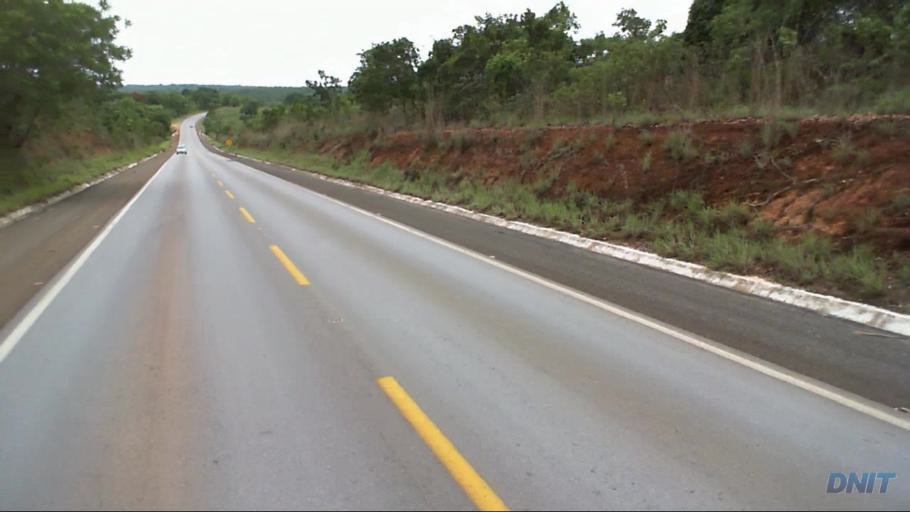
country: BR
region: Goias
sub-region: Uruacu
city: Uruacu
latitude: -14.7549
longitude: -49.0696
